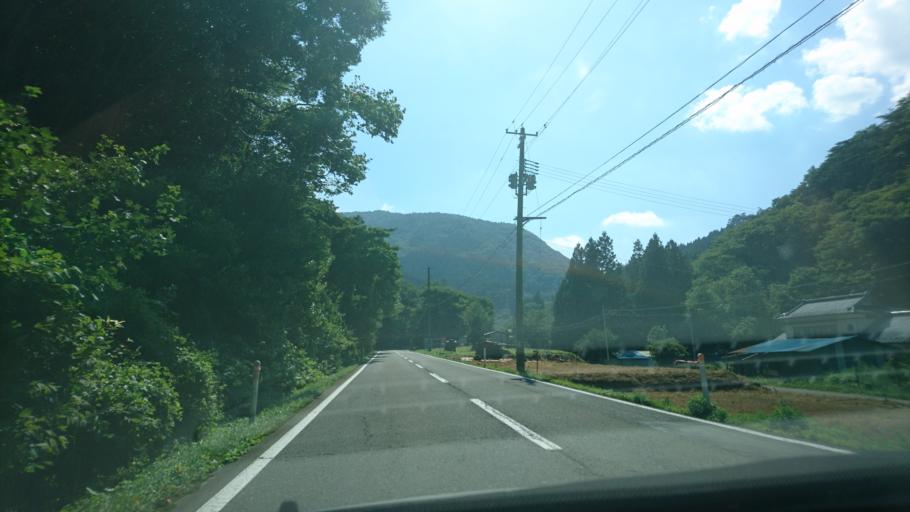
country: JP
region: Iwate
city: Ofunato
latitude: 39.0300
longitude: 141.5174
